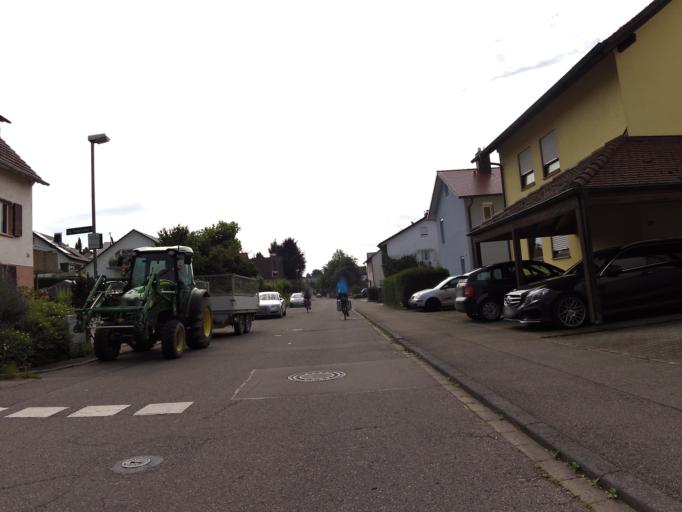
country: DE
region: Baden-Wuerttemberg
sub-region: Freiburg Region
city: Allensbach
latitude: 47.7205
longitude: 9.0568
